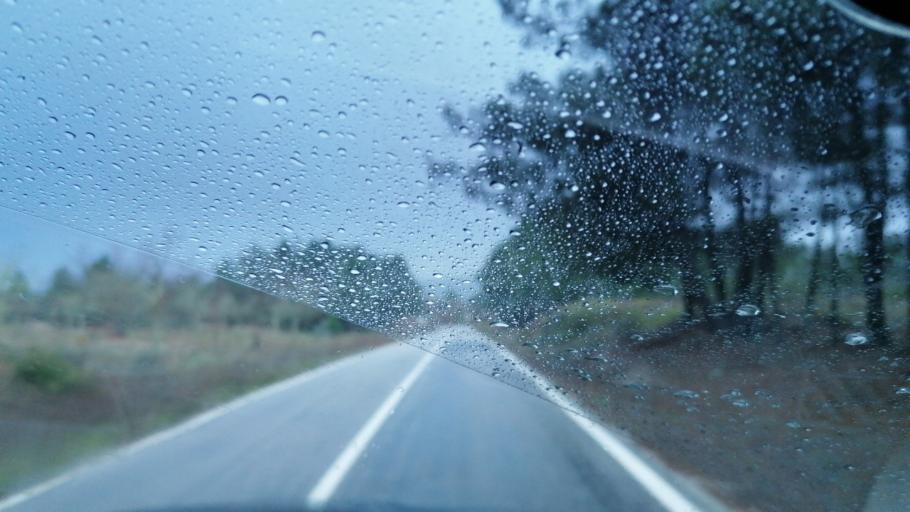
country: PT
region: Vila Real
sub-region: Murca
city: Murca
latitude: 41.4401
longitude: -7.5316
